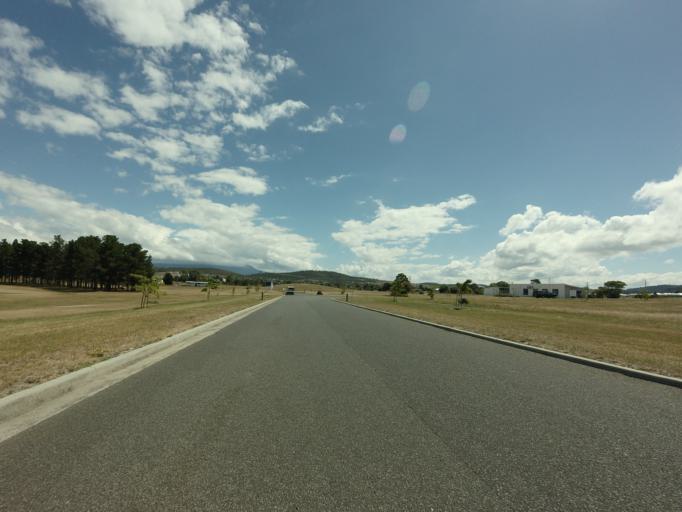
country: AU
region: Tasmania
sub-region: Clarence
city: Rokeby
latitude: -42.9075
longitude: 147.4546
